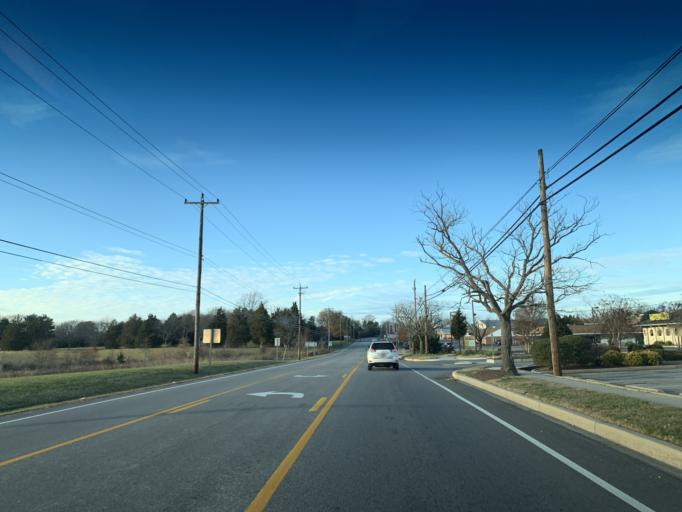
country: US
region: Maryland
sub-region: Kent County
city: Chestertown
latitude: 39.2248
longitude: -76.0705
